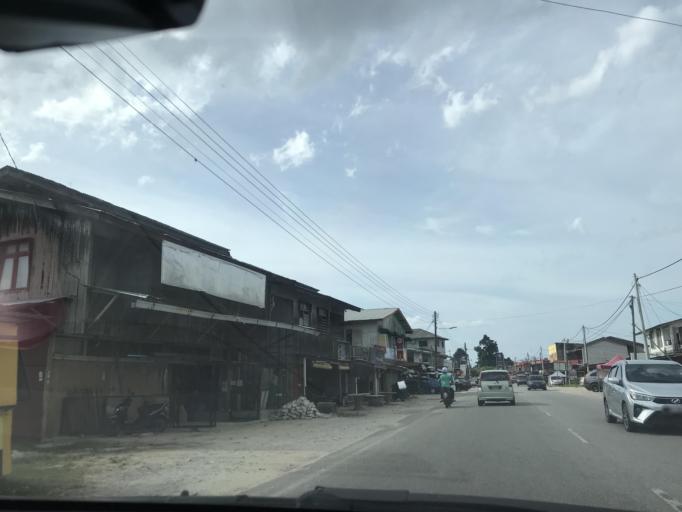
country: MY
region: Kelantan
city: Kota Bharu
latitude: 6.0948
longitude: 102.2302
